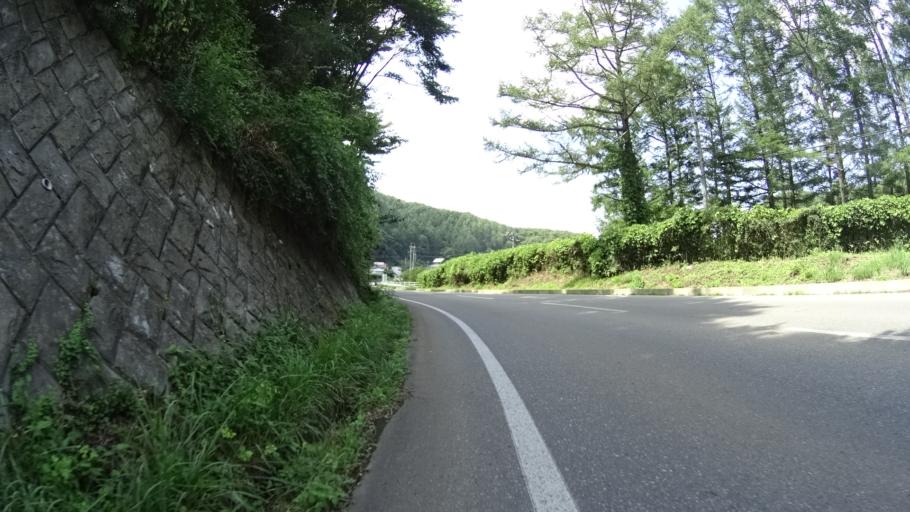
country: JP
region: Nagano
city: Saku
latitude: 36.0776
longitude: 138.4912
